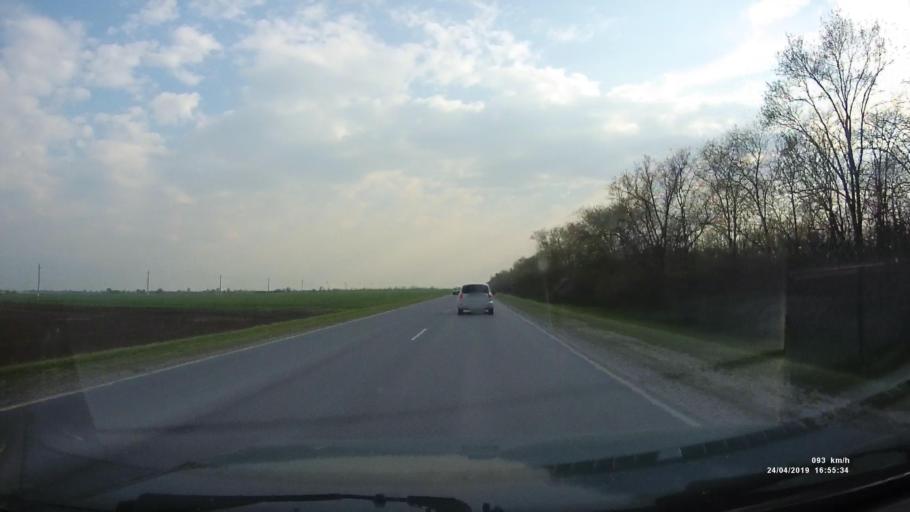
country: RU
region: Rostov
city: Proletarsk
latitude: 46.6625
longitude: 41.6866
